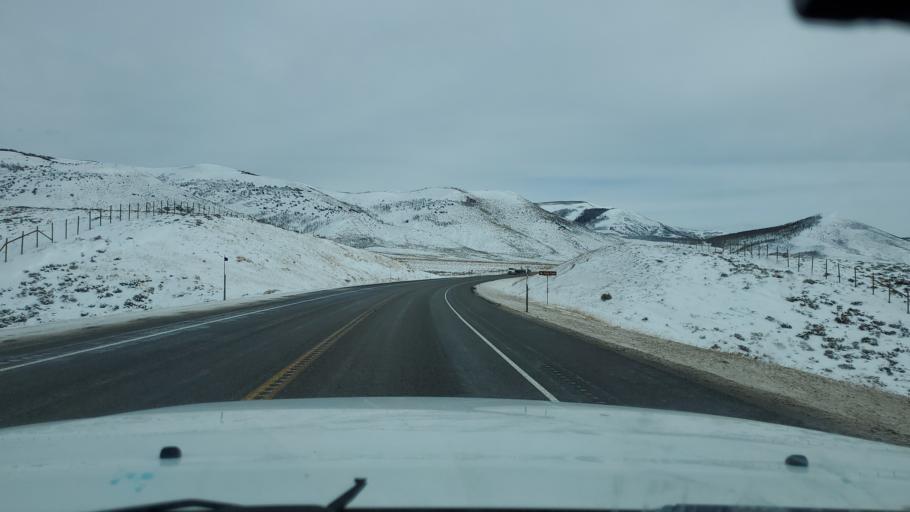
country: US
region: Utah
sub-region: Wasatch County
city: Heber
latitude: 40.2309
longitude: -111.1252
